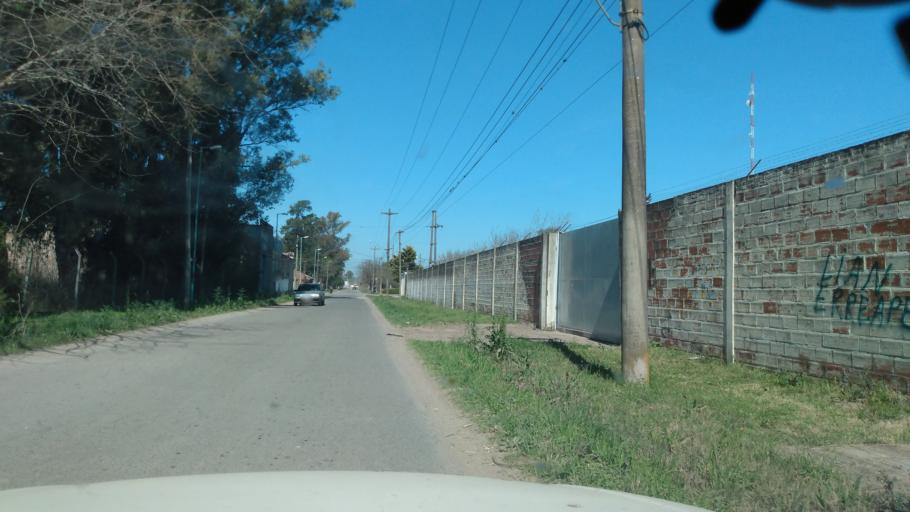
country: AR
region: Buenos Aires
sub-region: Partido de Lujan
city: Lujan
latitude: -34.5838
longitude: -59.1189
